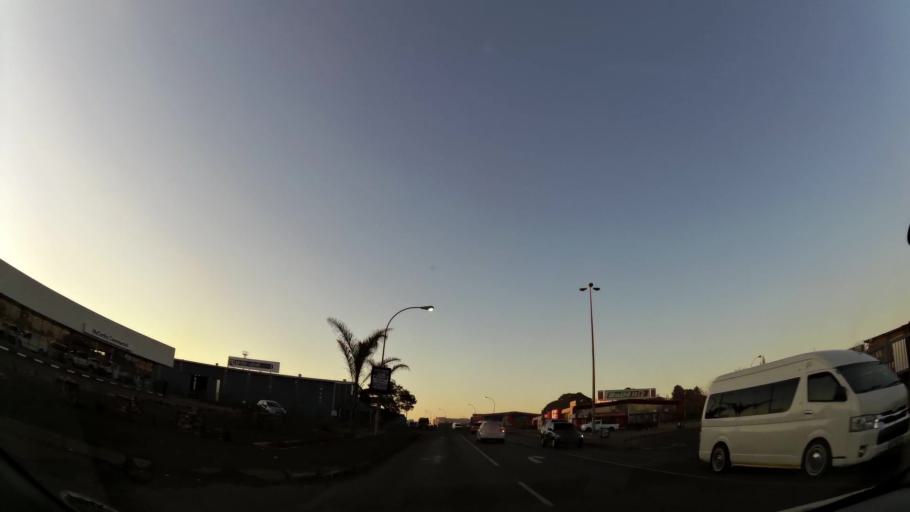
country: ZA
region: Mpumalanga
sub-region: Nkangala District Municipality
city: Witbank
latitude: -25.8818
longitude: 29.2073
